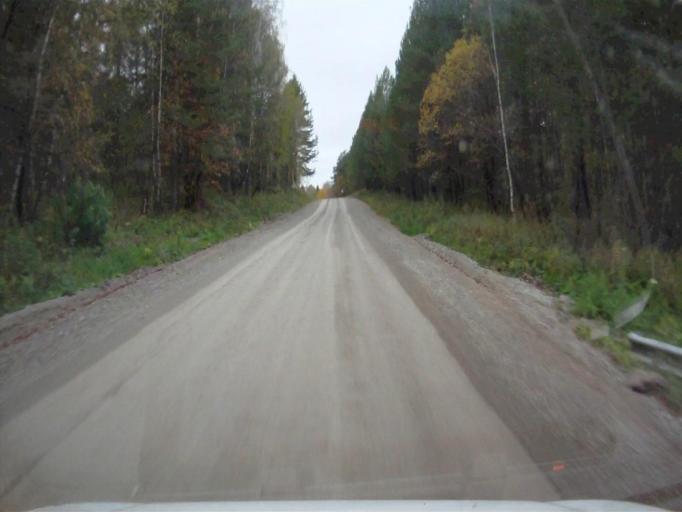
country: RU
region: Chelyabinsk
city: Nyazepetrovsk
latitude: 56.0614
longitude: 59.4492
